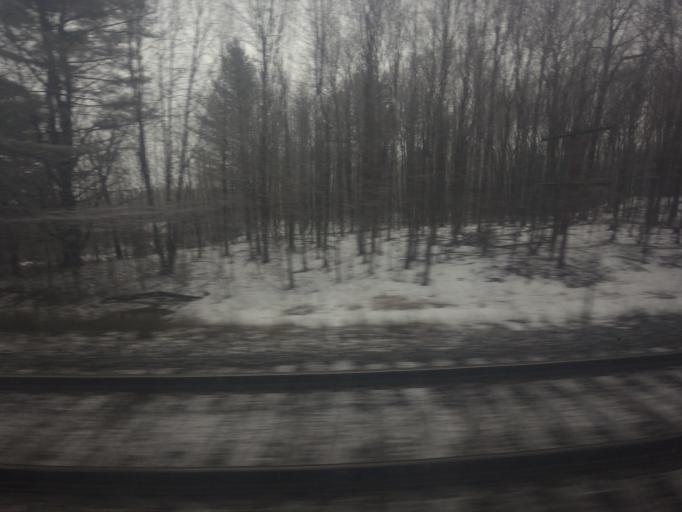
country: CA
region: Ontario
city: Brockville
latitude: 44.5609
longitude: -75.7843
